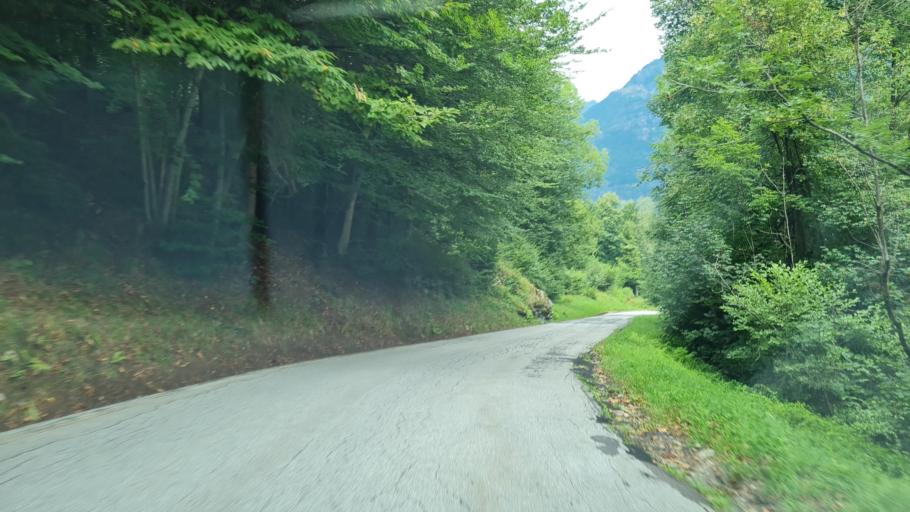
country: IT
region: Piedmont
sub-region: Provincia Verbano-Cusio-Ossola
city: Baceno
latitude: 46.2481
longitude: 8.3146
